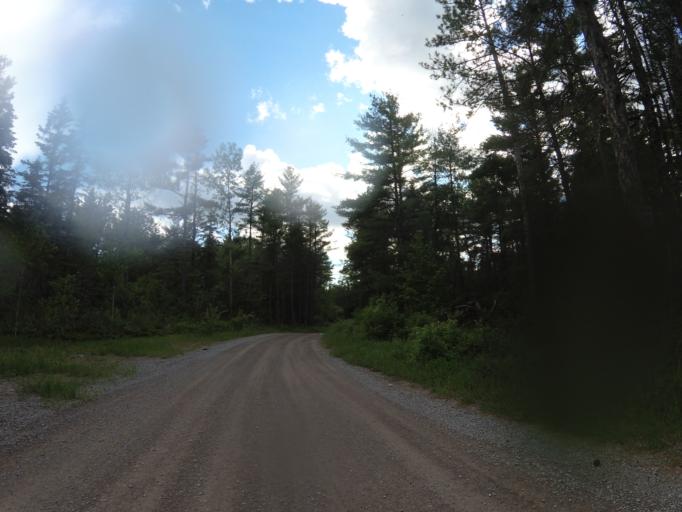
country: CA
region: Ontario
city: Renfrew
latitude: 45.1734
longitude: -76.9307
